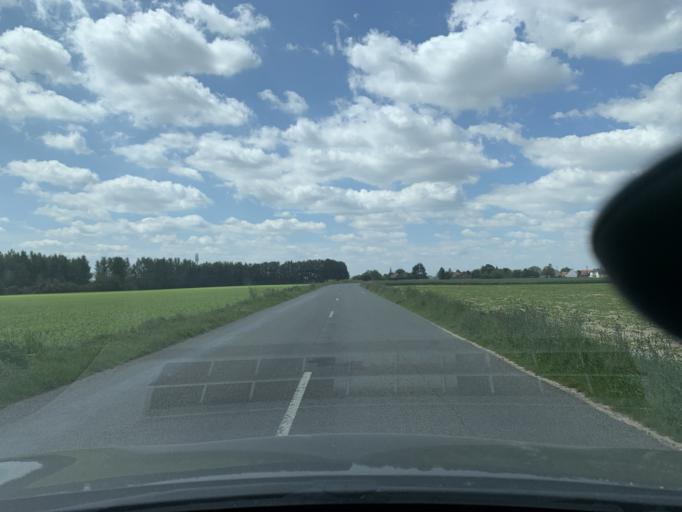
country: FR
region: Nord-Pas-de-Calais
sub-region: Departement du Pas-de-Calais
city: Ecourt-Saint-Quentin
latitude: 50.2588
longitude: 3.0863
